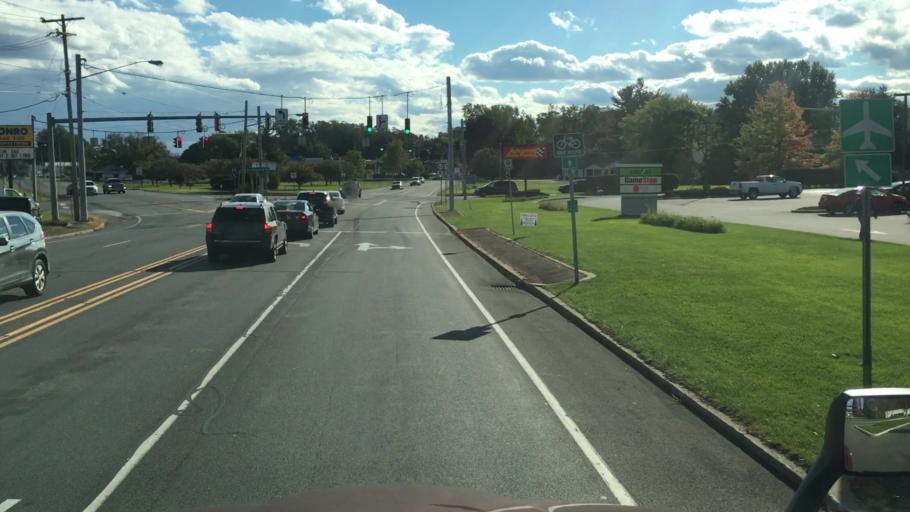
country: US
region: New York
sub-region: Schenectady County
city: Scotia
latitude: 42.8499
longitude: -73.9428
